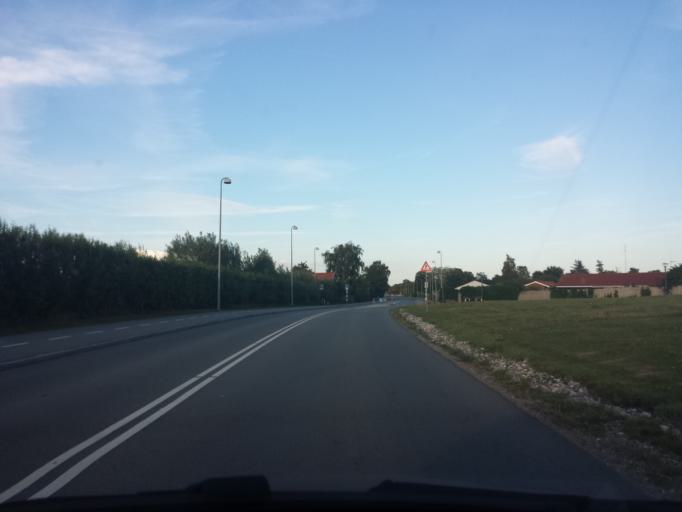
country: DK
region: Capital Region
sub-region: Egedal Kommune
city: Stenlose
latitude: 55.7664
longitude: 12.1775
